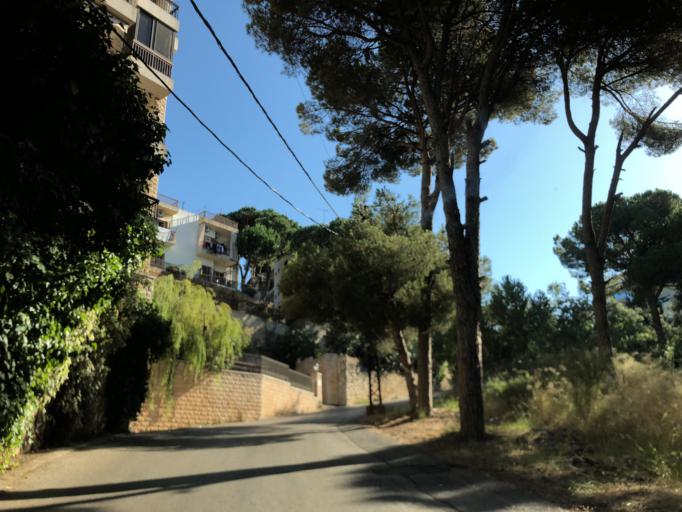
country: LB
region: Mont-Liban
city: Bhamdoun el Mhatta
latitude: 33.8882
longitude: 35.6614
